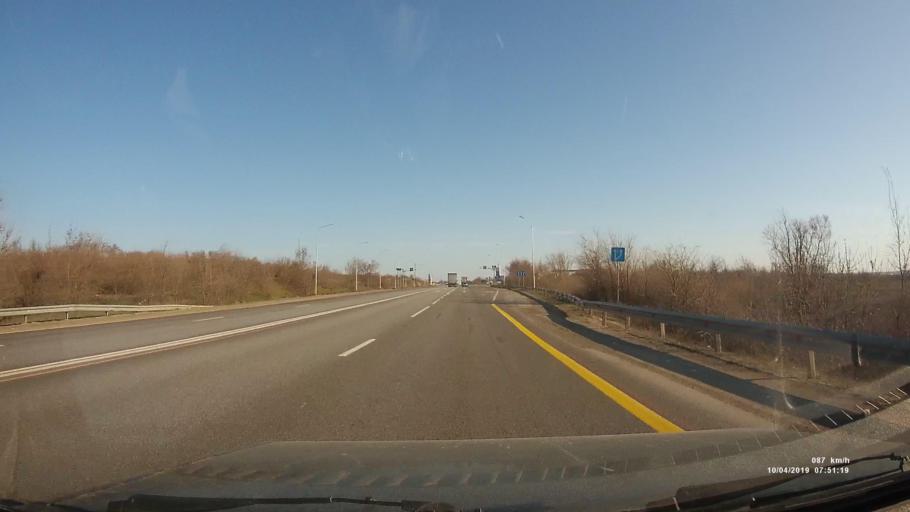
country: RU
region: Rostov
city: Kamensk-Shakhtinskiy
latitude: 48.2725
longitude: 40.2941
